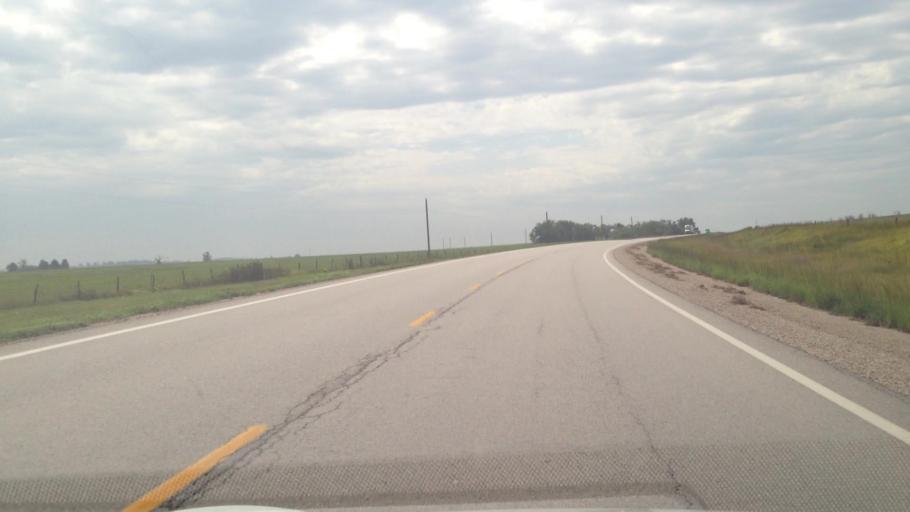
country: US
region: Kansas
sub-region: Anderson County
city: Garnett
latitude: 38.1900
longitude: -95.2414
